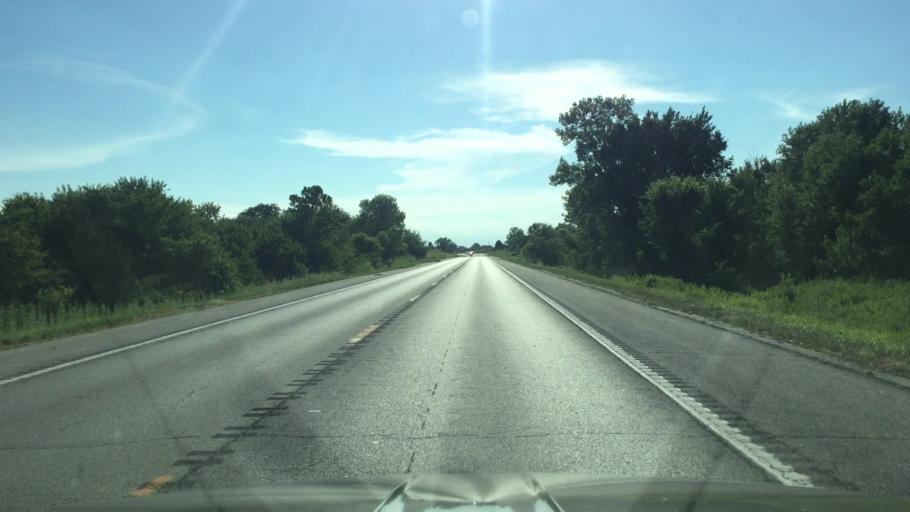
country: US
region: Missouri
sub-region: Pettis County
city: Sedalia
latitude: 38.6950
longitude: -93.1289
